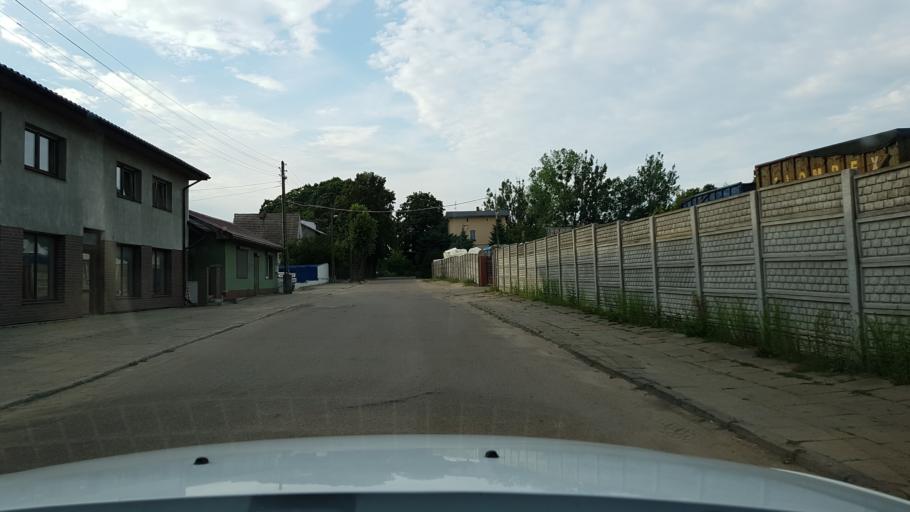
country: PL
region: West Pomeranian Voivodeship
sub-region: Powiat swidwinski
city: Polczyn-Zdroj
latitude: 53.7724
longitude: 16.0942
